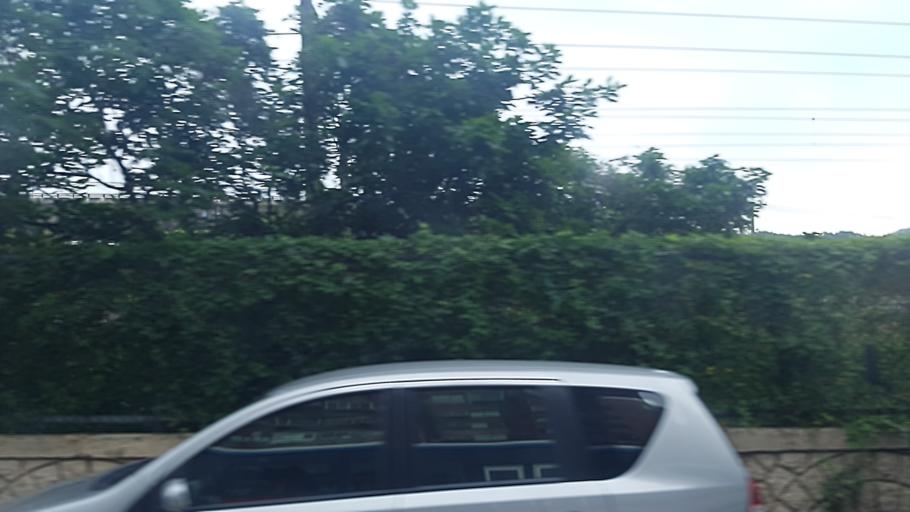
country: TW
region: Taiwan
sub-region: Hsinchu
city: Hsinchu
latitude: 24.7937
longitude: 120.9460
